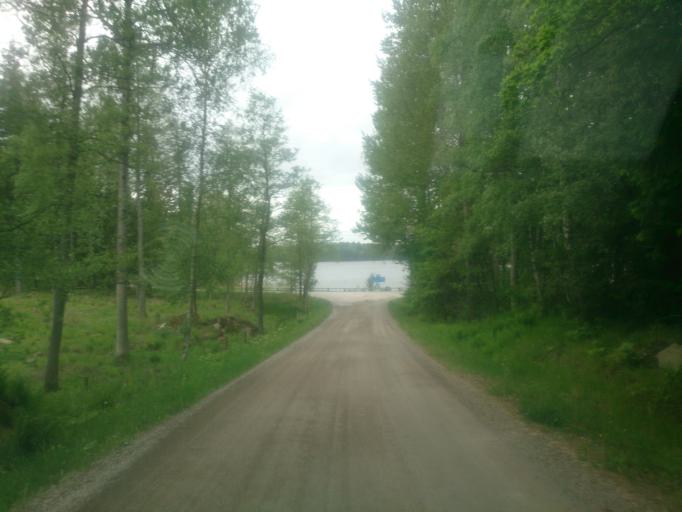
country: SE
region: OEstergoetland
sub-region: Atvidabergs Kommun
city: Atvidaberg
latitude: 58.2279
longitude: 16.0727
